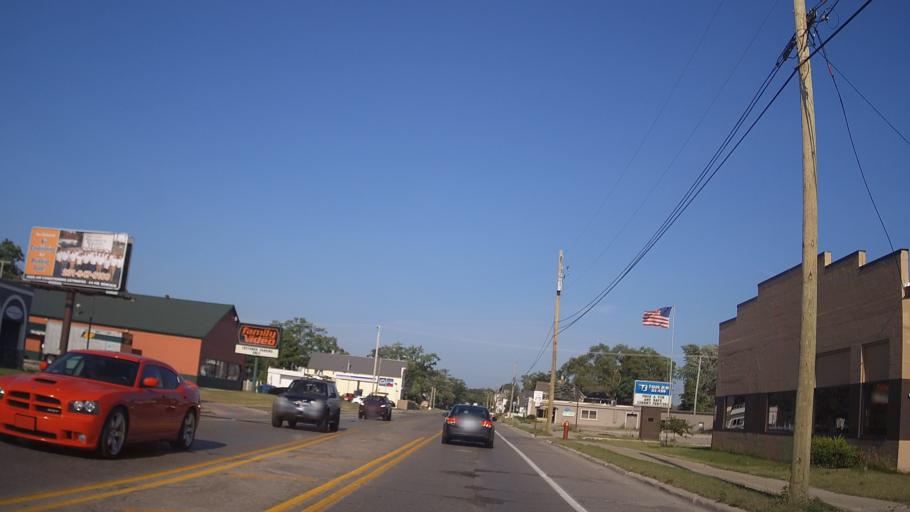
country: US
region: Michigan
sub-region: Grand Traverse County
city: Traverse City
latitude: 44.7594
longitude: -85.6151
